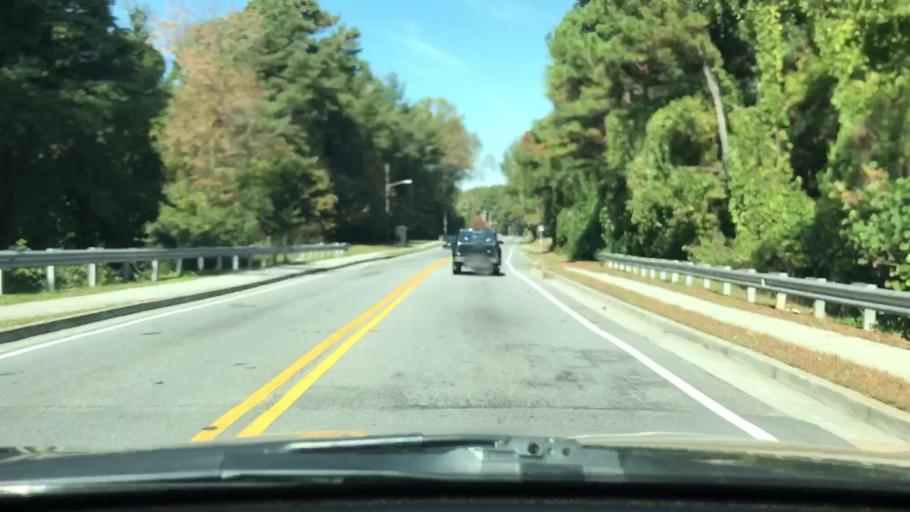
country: US
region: Georgia
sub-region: Gwinnett County
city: Norcross
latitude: 33.9256
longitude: -84.1937
